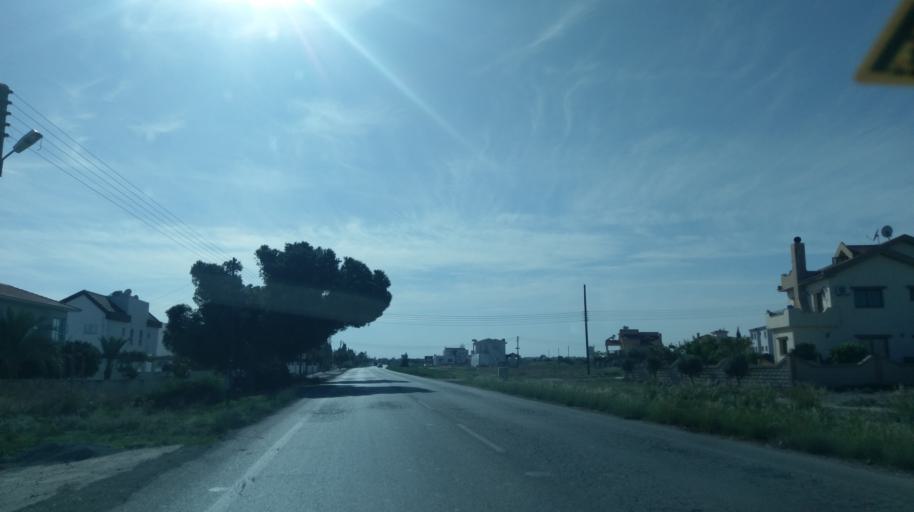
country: CY
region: Ammochostos
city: Trikomo
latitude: 35.3015
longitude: 33.9393
